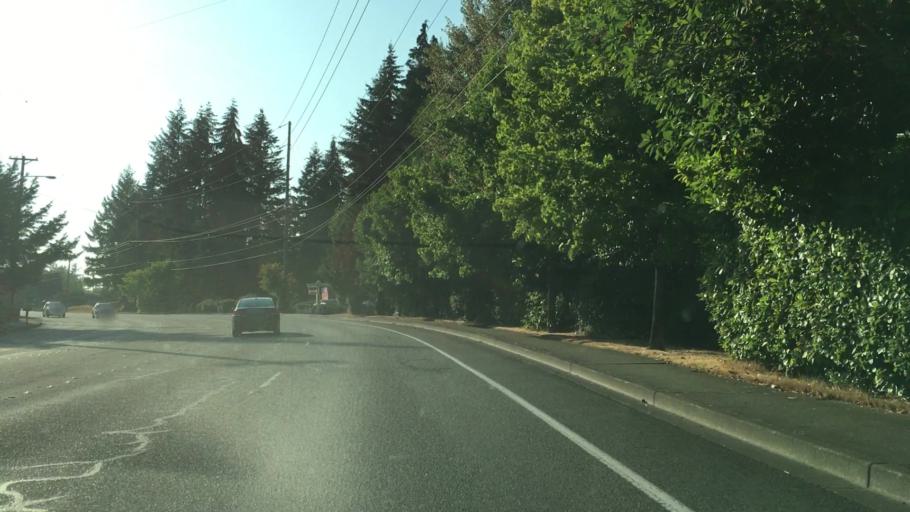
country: US
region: Washington
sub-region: Pierce County
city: Fife Heights
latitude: 47.2824
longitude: -122.3463
